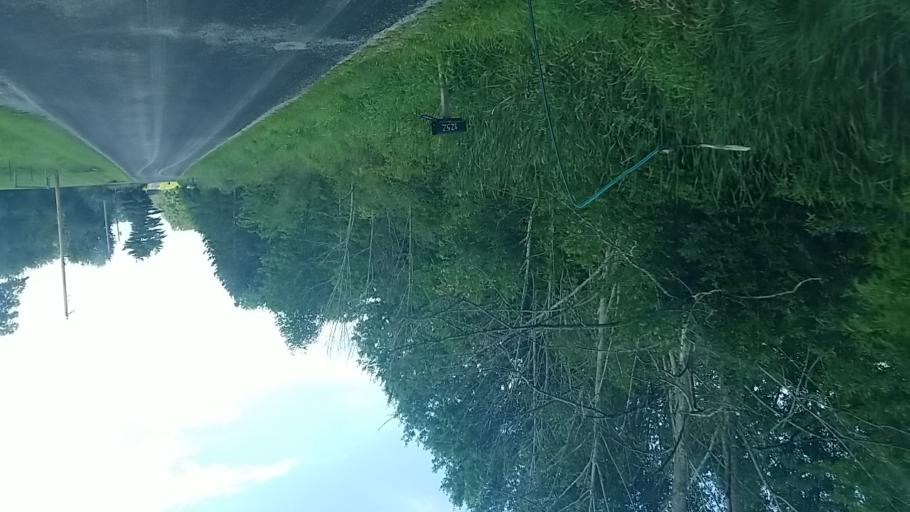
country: US
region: Ohio
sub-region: Wayne County
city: West Salem
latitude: 40.8787
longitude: -82.1926
